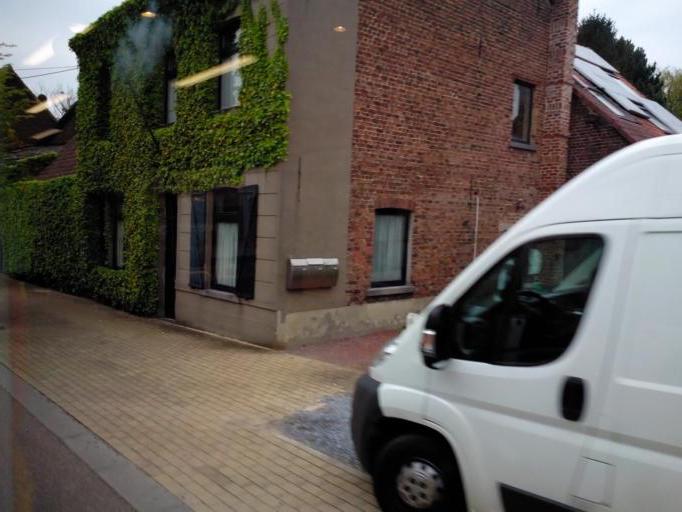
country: BE
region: Flanders
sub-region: Provincie Vlaams-Brabant
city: Kortenberg
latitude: 50.8837
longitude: 4.5448
